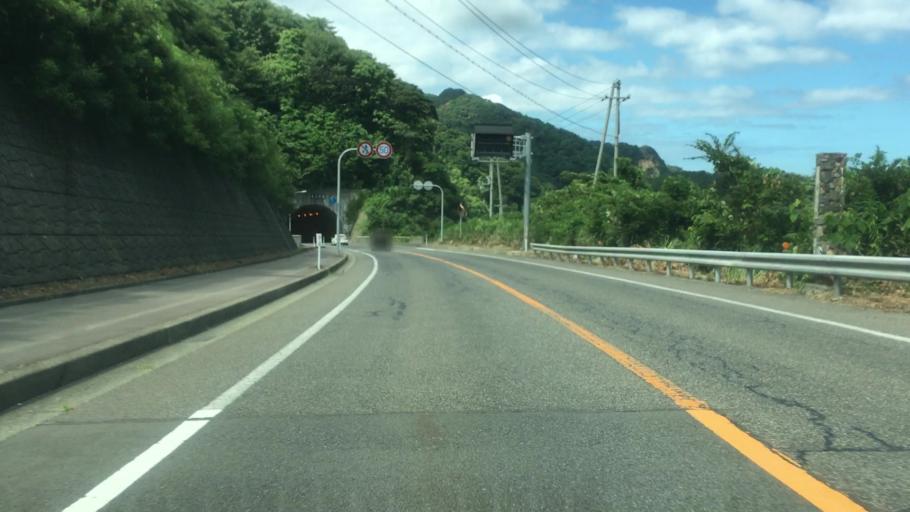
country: JP
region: Tottori
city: Tottori
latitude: 35.6196
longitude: 134.4184
